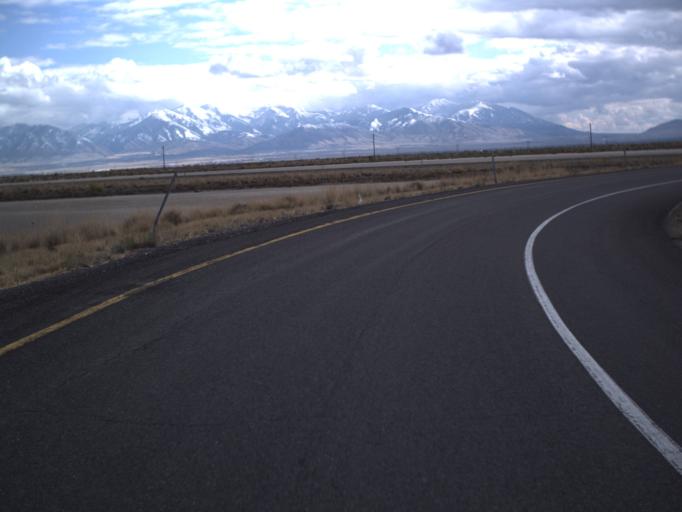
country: US
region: Utah
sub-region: Tooele County
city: Grantsville
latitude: 40.7069
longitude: -112.5244
